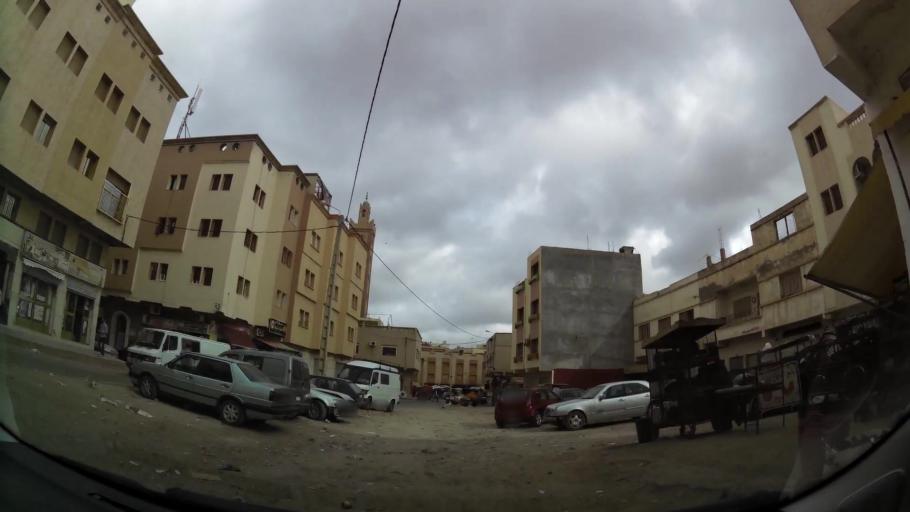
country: MA
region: Oriental
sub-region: Nador
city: Nador
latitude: 35.1694
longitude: -2.9386
